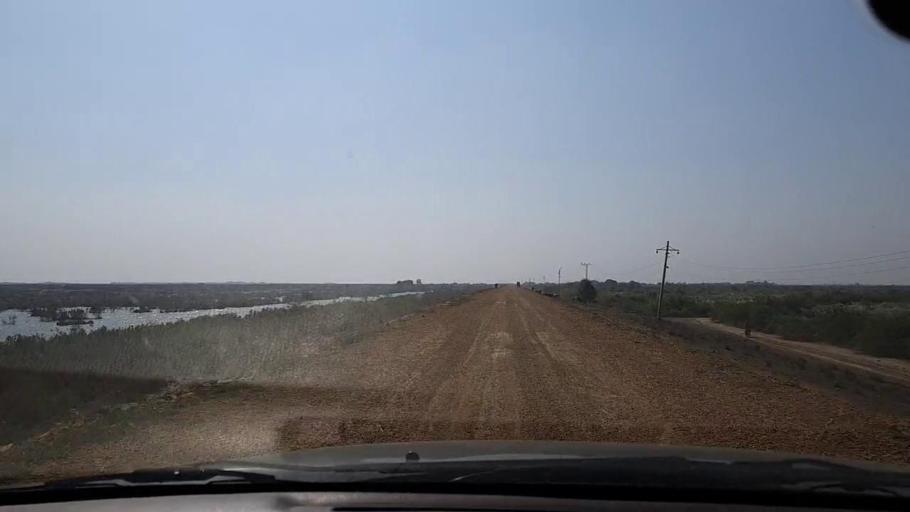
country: PK
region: Sindh
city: Chuhar Jamali
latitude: 24.4609
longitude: 67.8793
